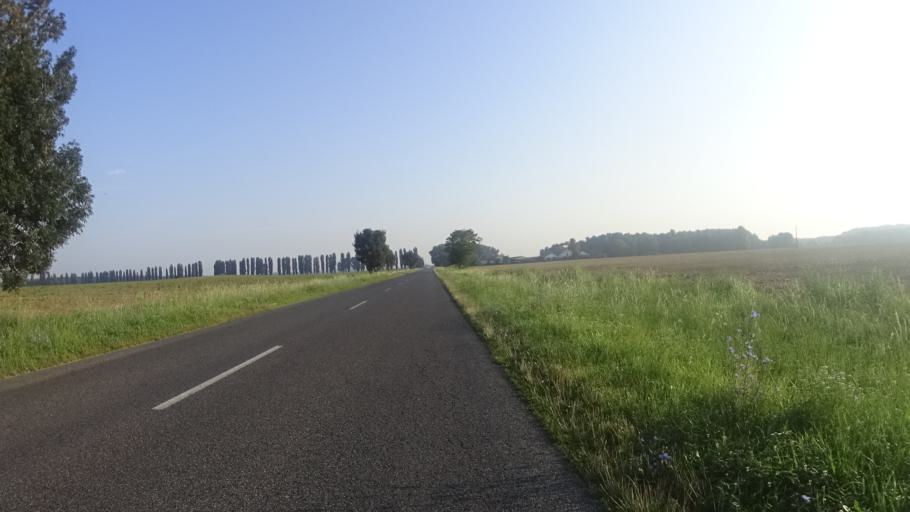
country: HU
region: Zala
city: Zalakomar
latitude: 46.6096
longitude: 17.1784
